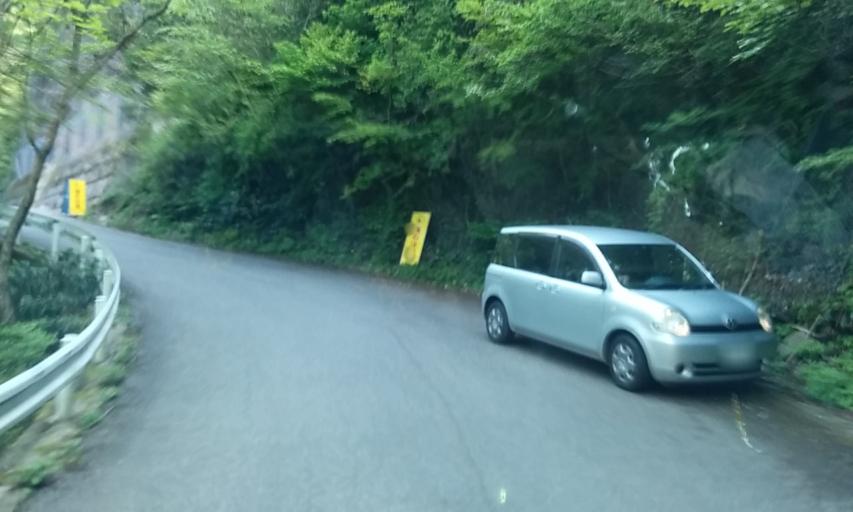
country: JP
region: Ehime
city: Niihama
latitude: 33.8716
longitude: 133.2966
